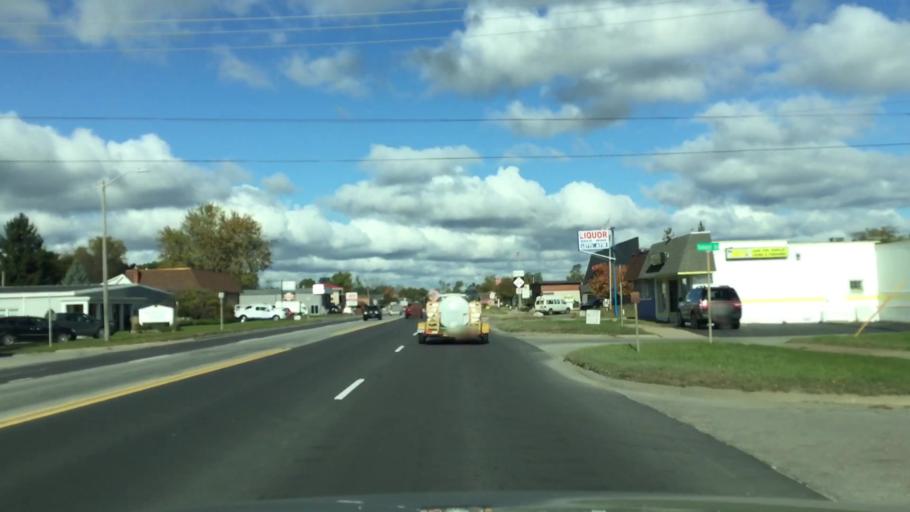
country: US
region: Michigan
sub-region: Oakland County
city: Oxford
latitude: 42.8148
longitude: -83.2558
